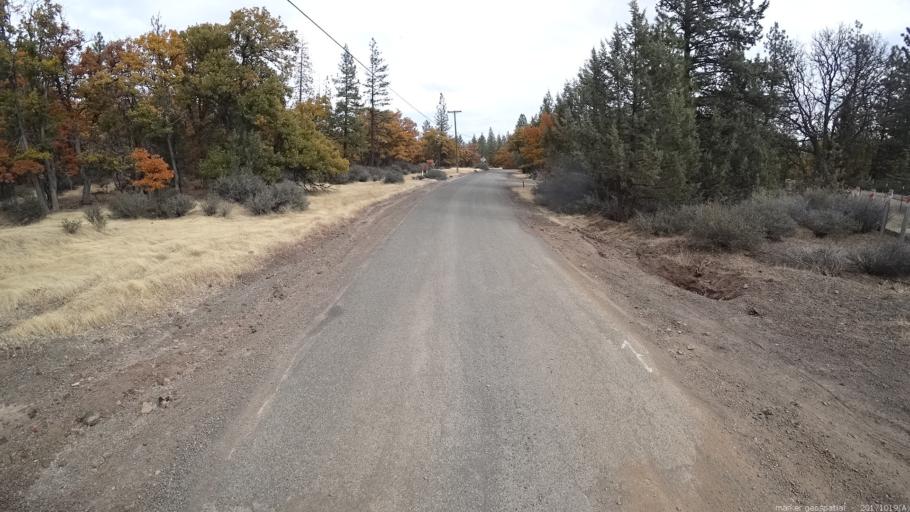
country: US
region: California
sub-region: Shasta County
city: Burney
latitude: 41.0603
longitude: -121.5395
